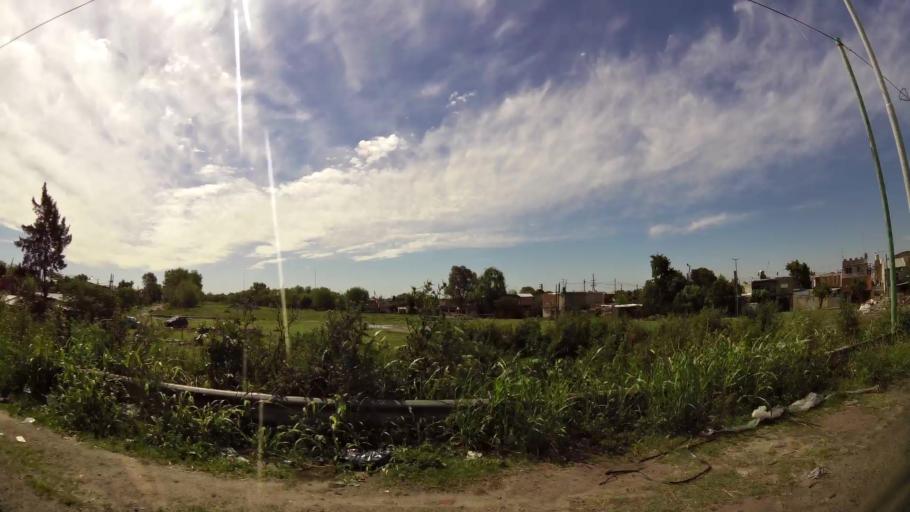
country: AR
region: Buenos Aires
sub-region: Partido de Almirante Brown
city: Adrogue
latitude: -34.7873
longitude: -58.3049
